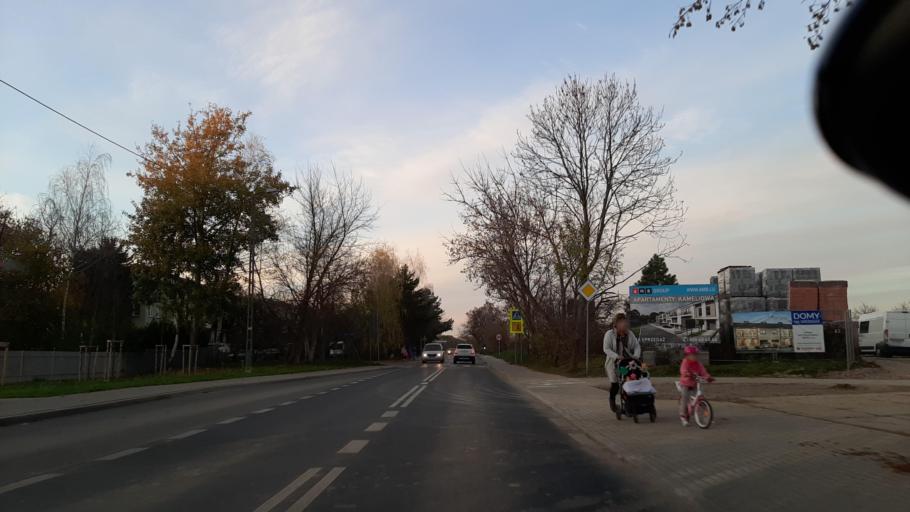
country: PL
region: Lublin Voivodeship
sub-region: Powiat lubelski
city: Lublin
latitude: 51.2716
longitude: 22.5108
